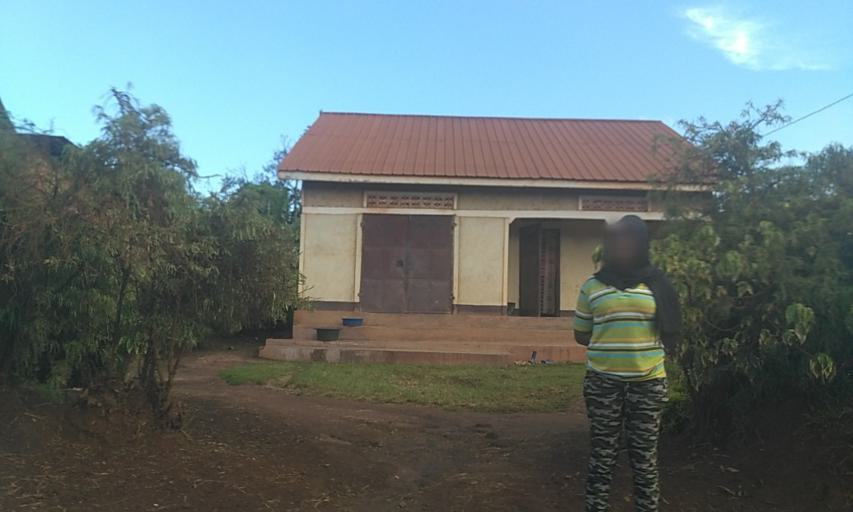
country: UG
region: Central Region
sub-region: Wakiso District
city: Kajansi
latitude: 0.2387
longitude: 32.4953
